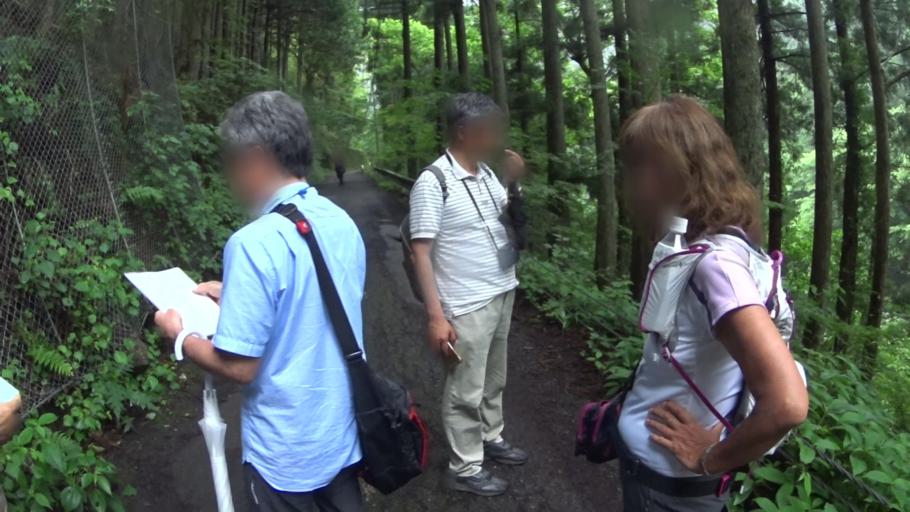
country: JP
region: Tokyo
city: Itsukaichi
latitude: 35.7928
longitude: 139.0621
